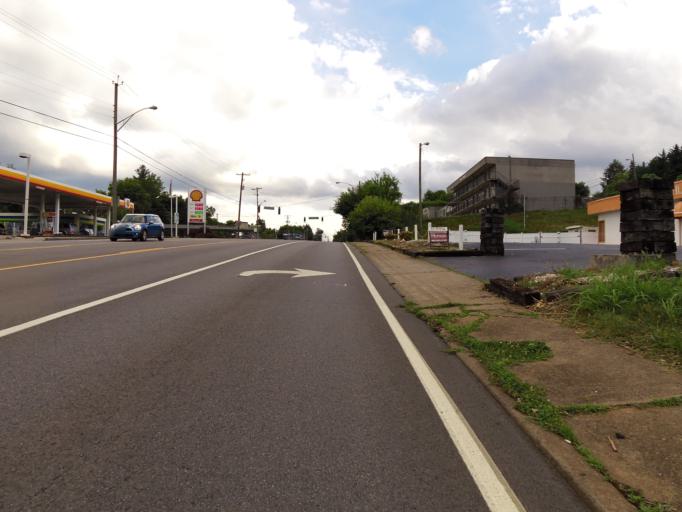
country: US
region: Tennessee
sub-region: Knox County
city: Knoxville
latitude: 35.9895
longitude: -83.9203
